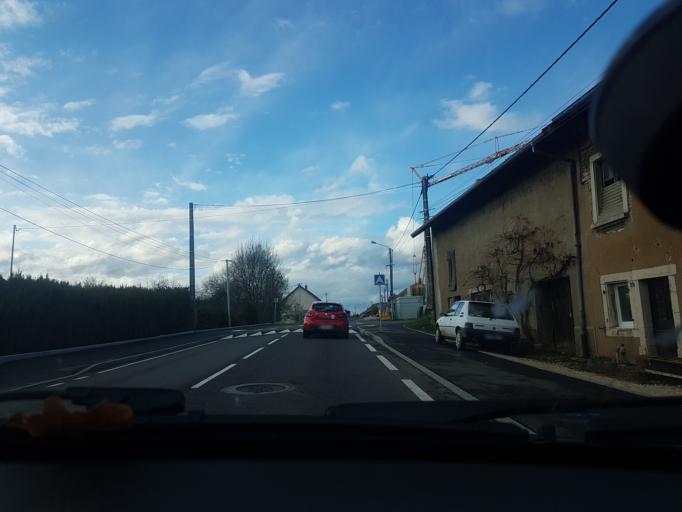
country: FR
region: Franche-Comte
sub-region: Territoire de Belfort
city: Essert
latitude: 47.6353
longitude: 6.8085
